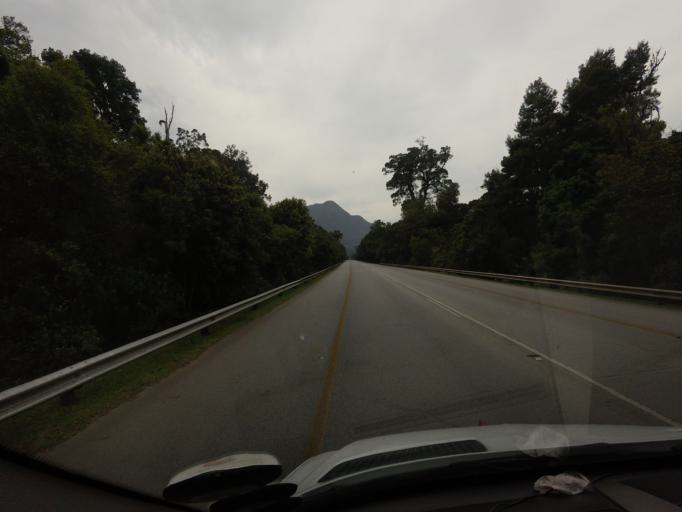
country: ZA
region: Eastern Cape
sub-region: Cacadu District Municipality
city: Kareedouw
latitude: -33.9683
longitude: 23.8601
